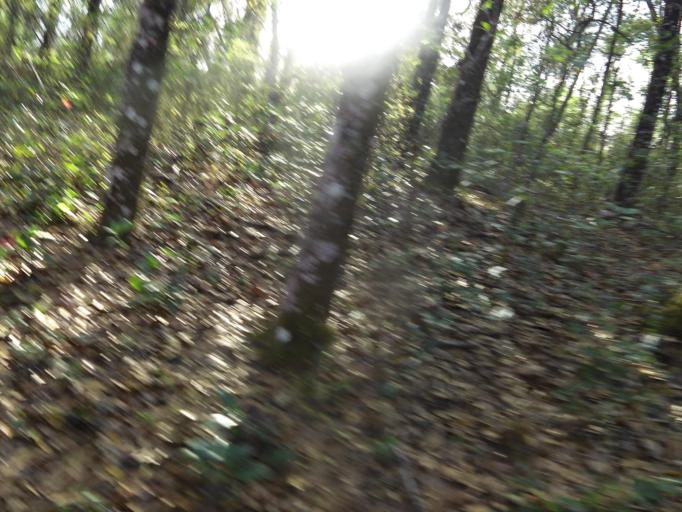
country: US
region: Florida
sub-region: Clay County
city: Middleburg
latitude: 30.1497
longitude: -81.9542
